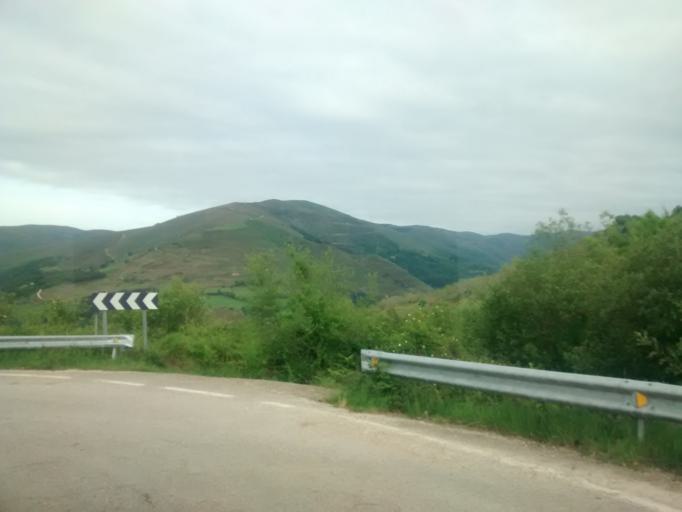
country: ES
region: Cantabria
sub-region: Provincia de Cantabria
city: San Vicente de la Barquera
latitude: 43.2503
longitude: -4.4267
